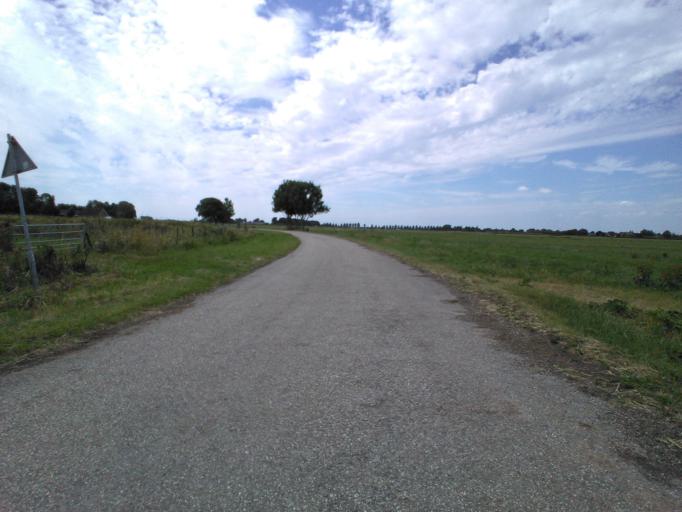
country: NL
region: South Holland
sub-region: Gemeente Giessenlanden
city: Giessenburg
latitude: 51.8837
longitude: 4.8712
